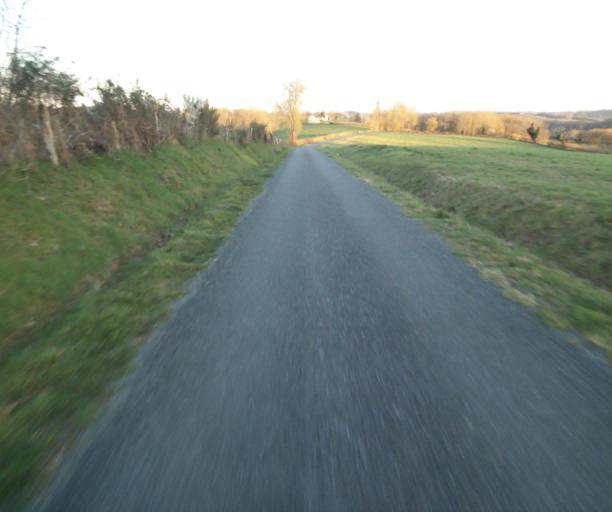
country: FR
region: Limousin
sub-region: Departement de la Correze
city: Uzerche
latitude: 45.3762
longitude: 1.6064
